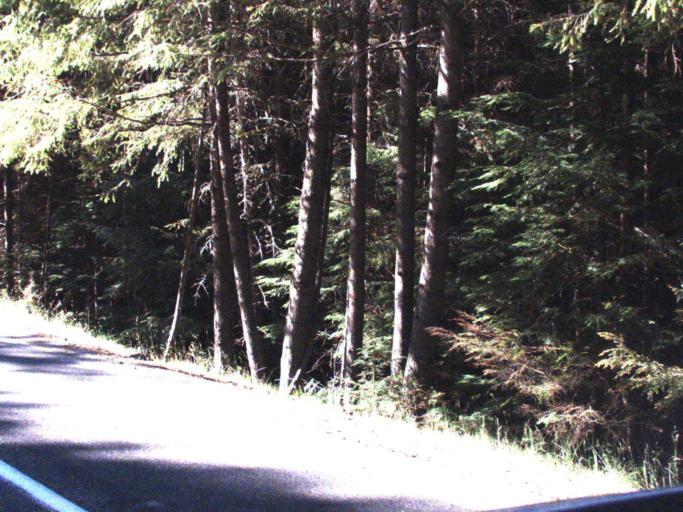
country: US
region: Washington
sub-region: King County
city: Riverbend
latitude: 47.0919
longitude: -121.5847
